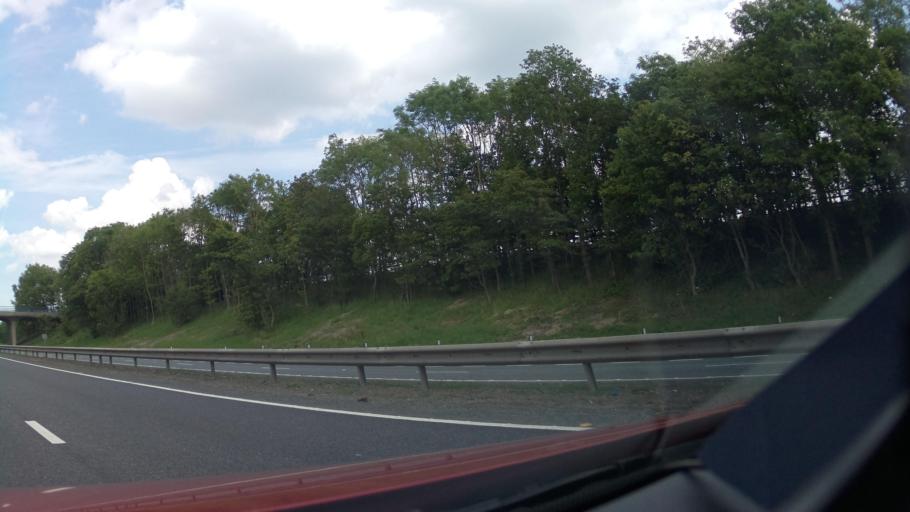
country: GB
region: England
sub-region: Redcar and Cleveland
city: Thornaby-on-Tees
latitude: 54.4977
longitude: -1.2955
